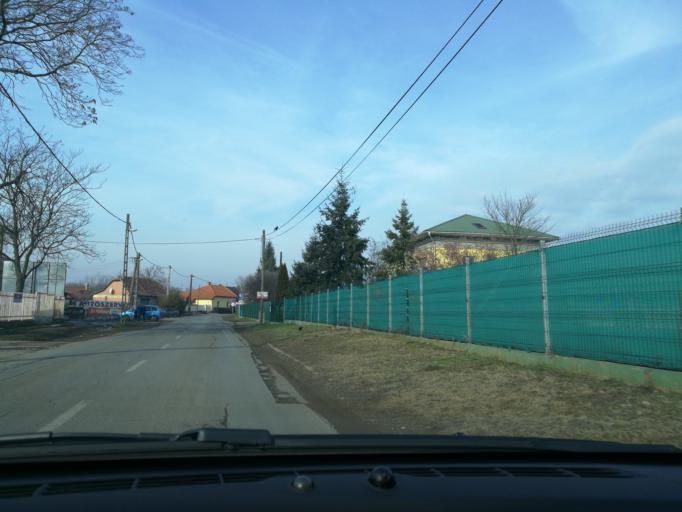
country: HU
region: Szabolcs-Szatmar-Bereg
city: Nyiregyhaza
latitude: 47.9648
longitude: 21.7333
